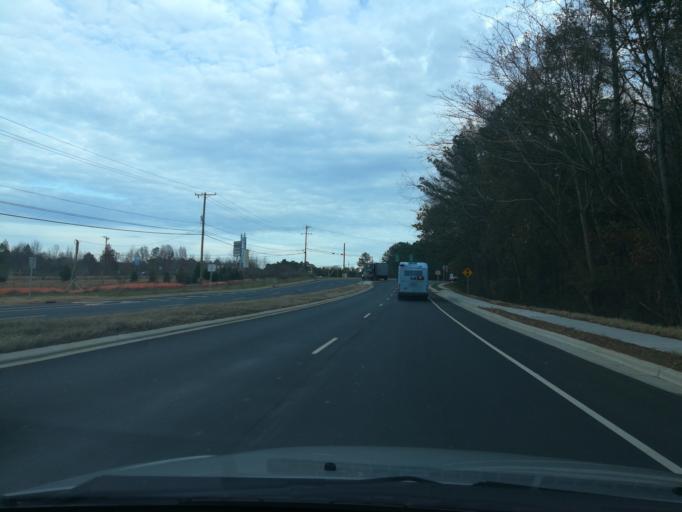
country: US
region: North Carolina
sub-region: Orange County
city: Chapel Hill
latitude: 35.9694
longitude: -79.0638
